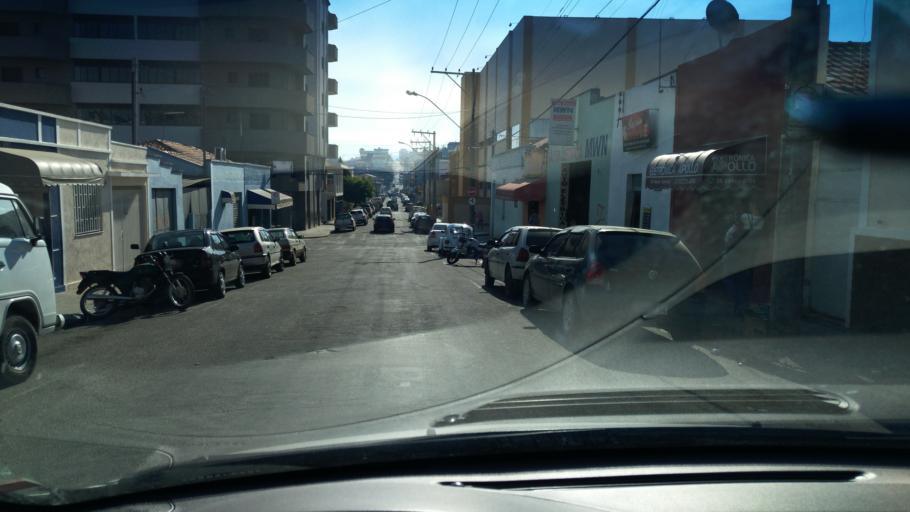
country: BR
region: Minas Gerais
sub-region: Andradas
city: Andradas
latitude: -22.0751
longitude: -46.5746
